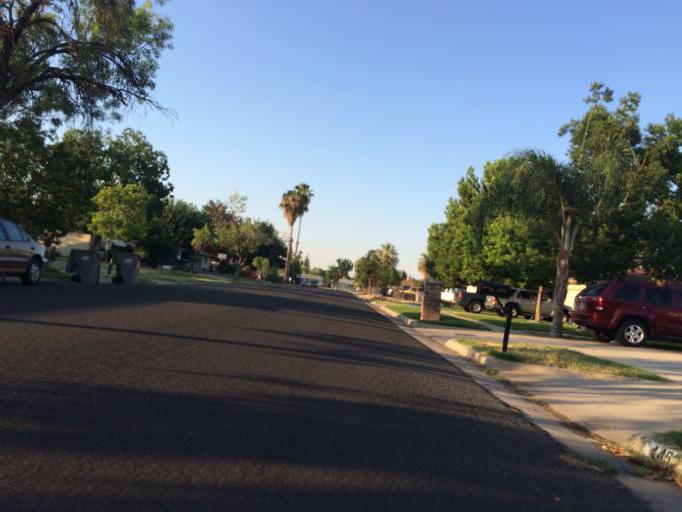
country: US
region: California
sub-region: Fresno County
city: Tarpey Village
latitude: 36.7987
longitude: -119.6916
